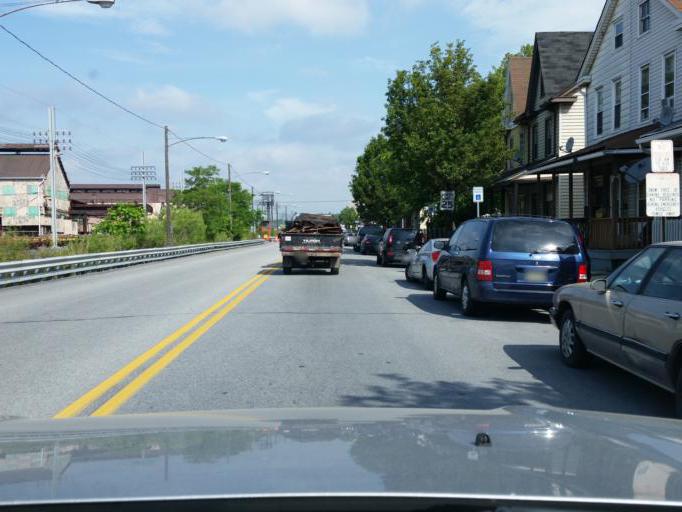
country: US
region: Pennsylvania
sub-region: Dauphin County
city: Enhaut
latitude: 40.2253
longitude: -76.8281
